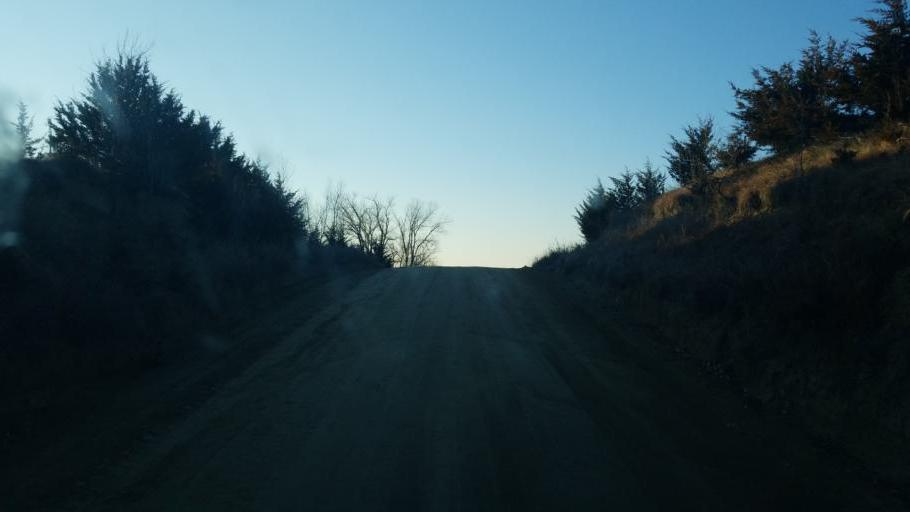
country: US
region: Nebraska
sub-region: Knox County
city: Center
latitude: 42.5602
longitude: -97.7986
